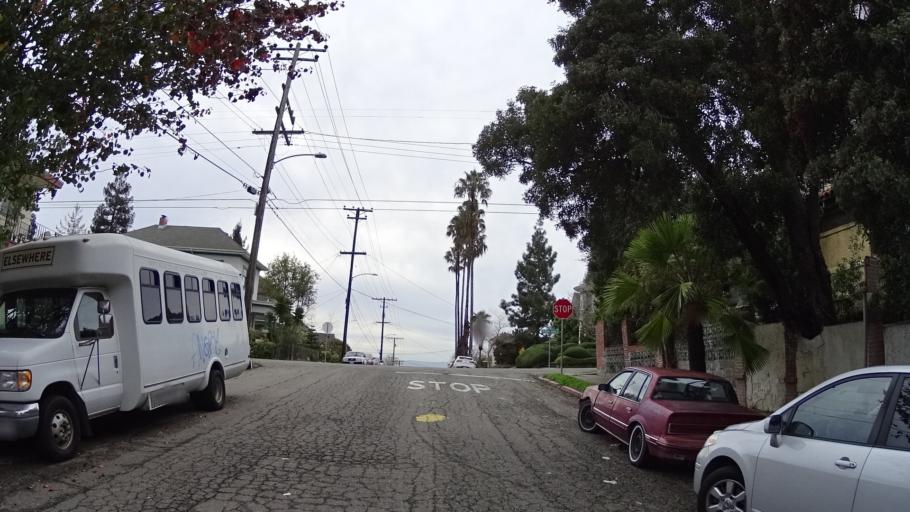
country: US
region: California
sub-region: Alameda County
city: Piedmont
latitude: 37.8009
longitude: -122.2356
